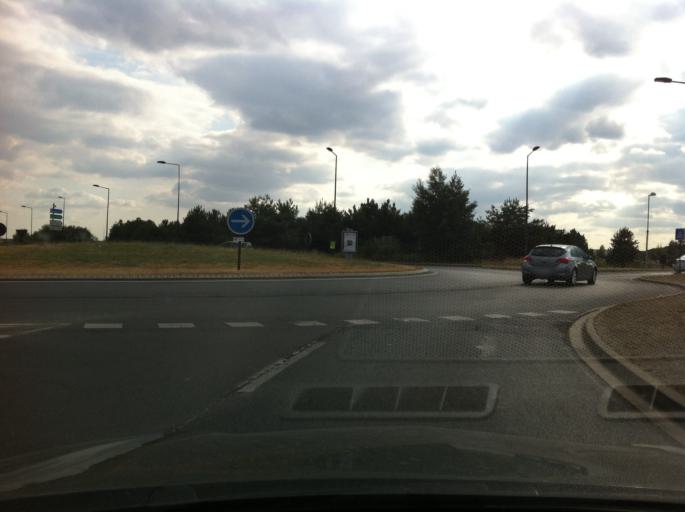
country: FR
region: Ile-de-France
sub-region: Departement de Seine-et-Marne
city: Lieusaint
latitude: 48.6225
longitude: 2.5580
